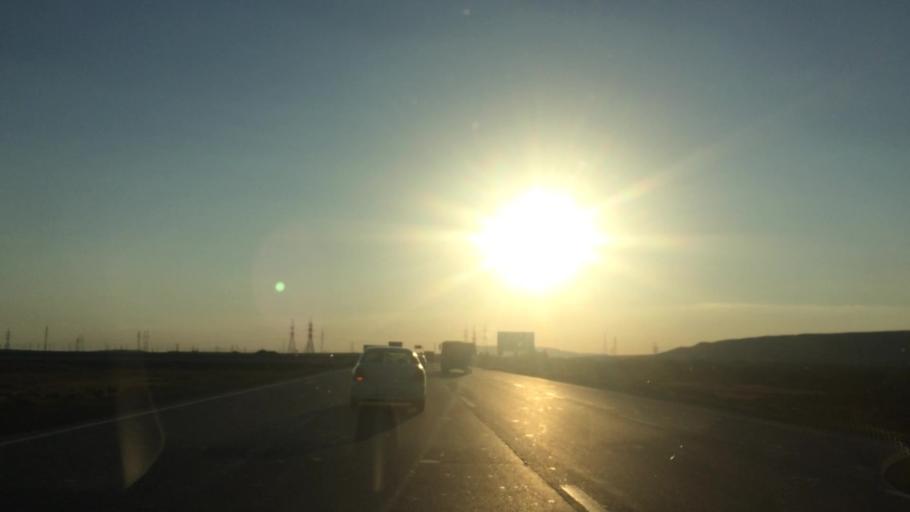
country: AZ
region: Baki
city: Qobustan
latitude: 39.9649
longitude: 49.4039
